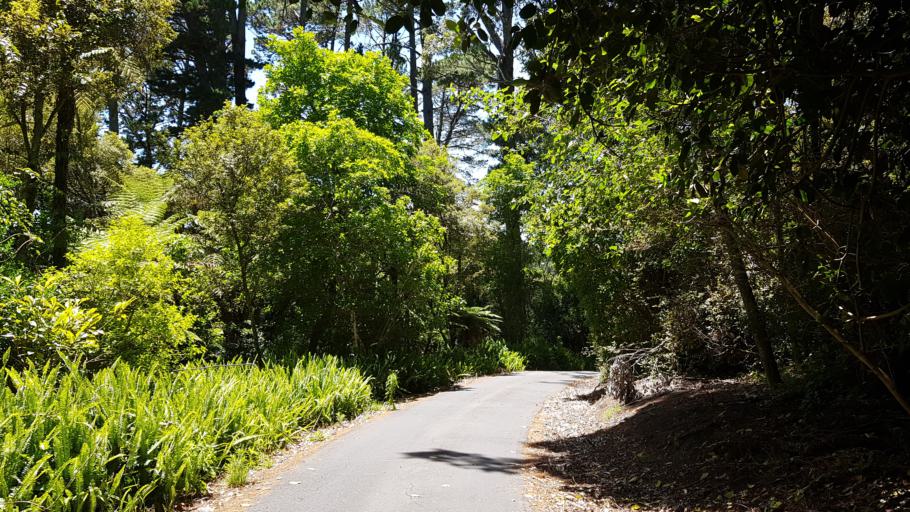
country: NZ
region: Auckland
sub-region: Auckland
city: North Shore
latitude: -36.8210
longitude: 174.7194
